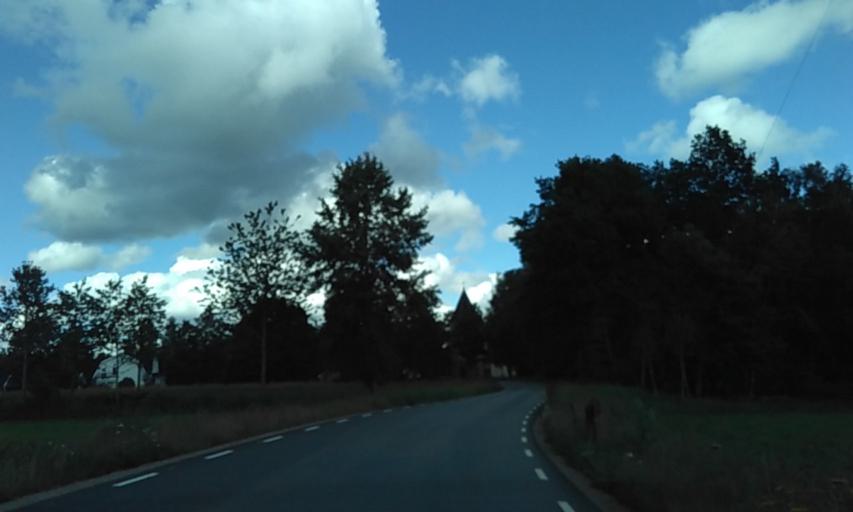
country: SE
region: Vaestra Goetaland
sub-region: Vargarda Kommun
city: Vargarda
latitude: 57.9869
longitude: 12.9283
